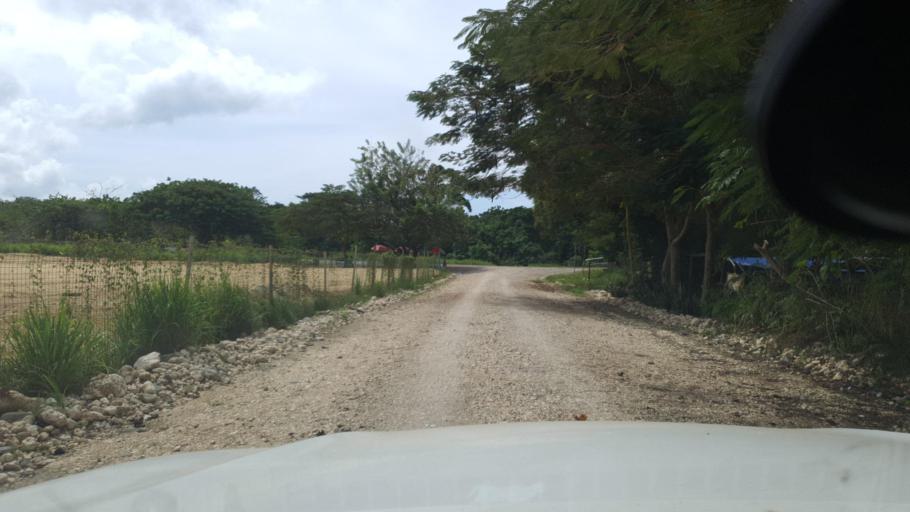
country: SB
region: Guadalcanal
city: Honiara
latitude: -9.4135
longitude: 159.8935
